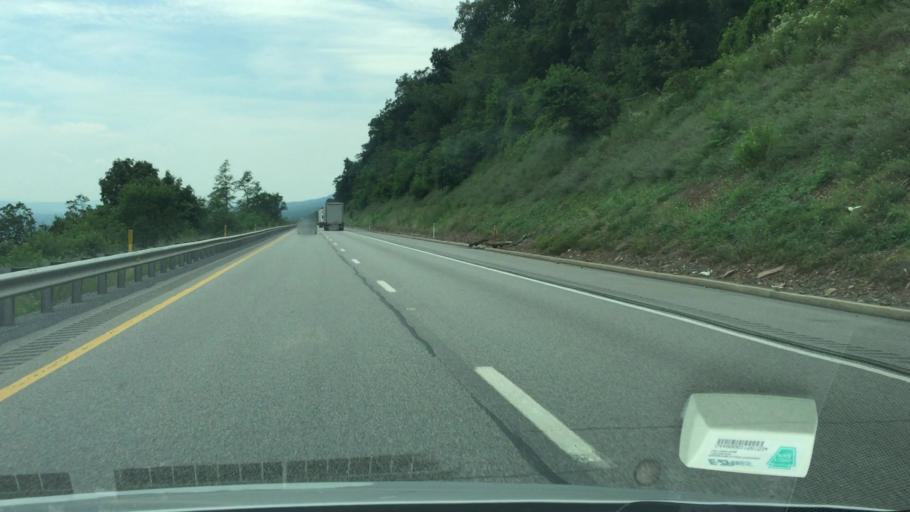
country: US
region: Pennsylvania
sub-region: Bedford County
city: Earlston
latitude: 39.8600
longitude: -78.2664
